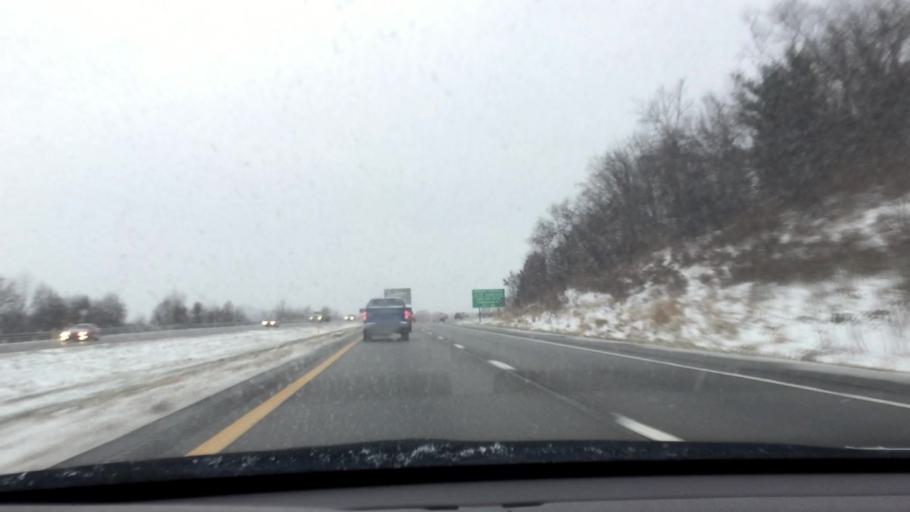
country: US
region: Pennsylvania
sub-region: Washington County
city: Canonsburg
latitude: 40.2859
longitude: -80.1671
